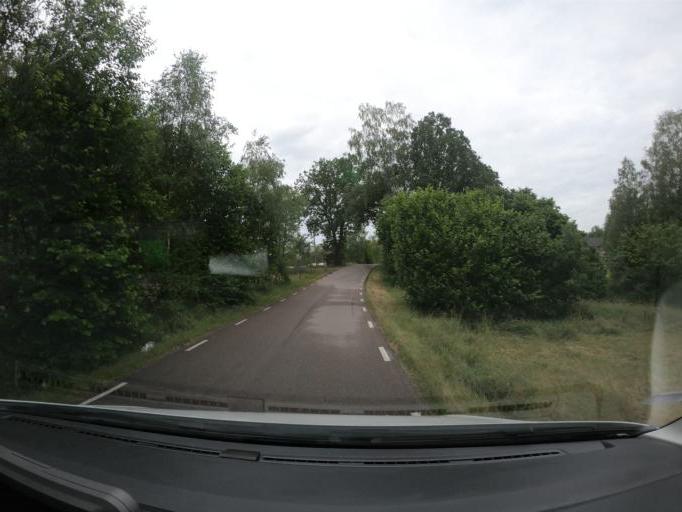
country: SE
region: Skane
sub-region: Orkelljunga Kommun
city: OErkelljunga
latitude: 56.2610
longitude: 13.1559
